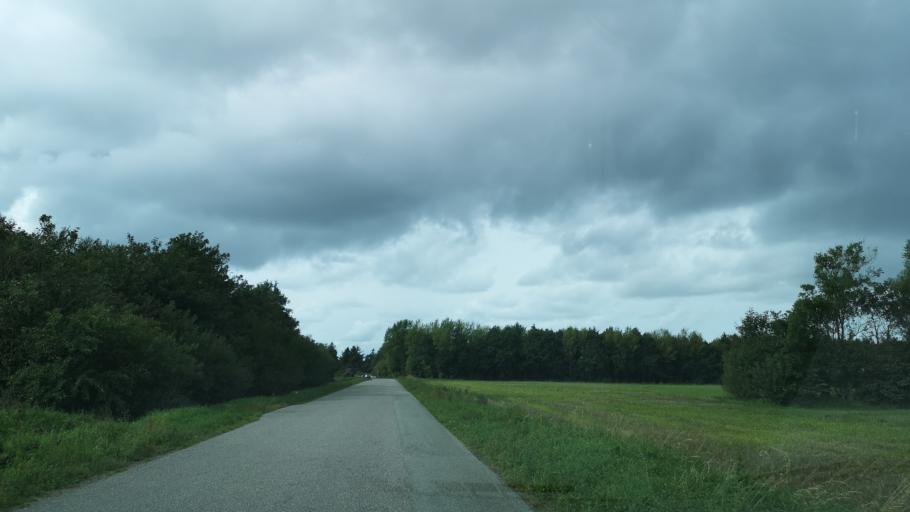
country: DK
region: South Denmark
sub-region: Varde Kommune
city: Oksbol
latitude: 55.8390
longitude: 8.2922
